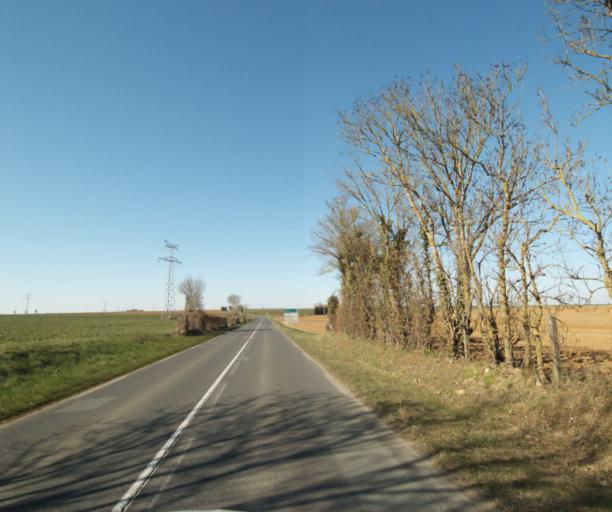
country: FR
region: Poitou-Charentes
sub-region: Departement des Deux-Sevres
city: Saint-Maxire
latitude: 46.3607
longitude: -0.4860
